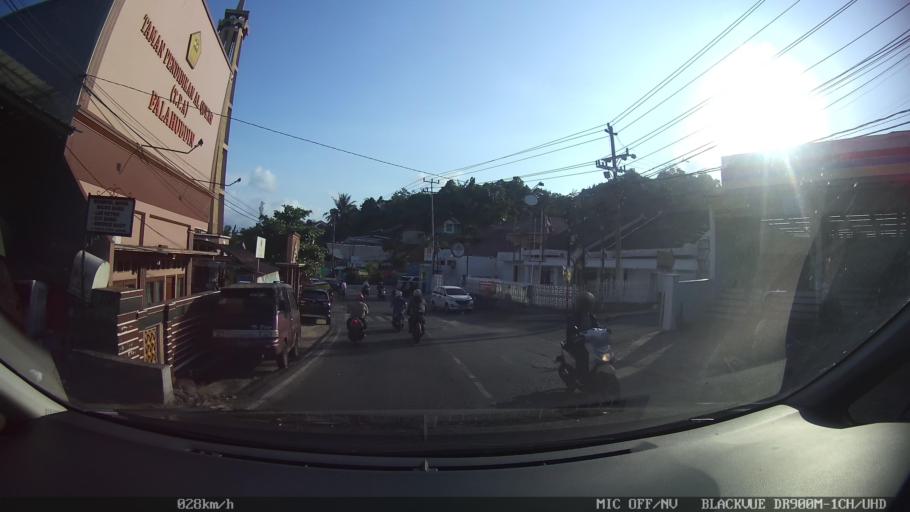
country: ID
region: Lampung
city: Bandarlampung
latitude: -5.4063
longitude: 105.2492
